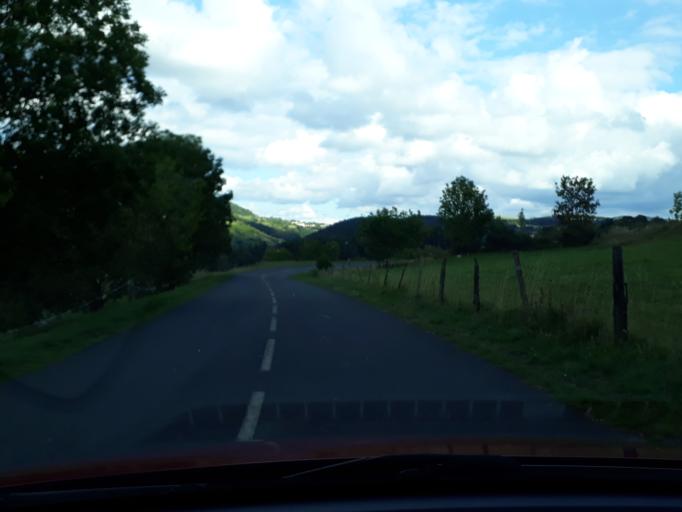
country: FR
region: Languedoc-Roussillon
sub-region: Departement de la Lozere
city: Langogne
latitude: 44.8186
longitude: 3.9318
